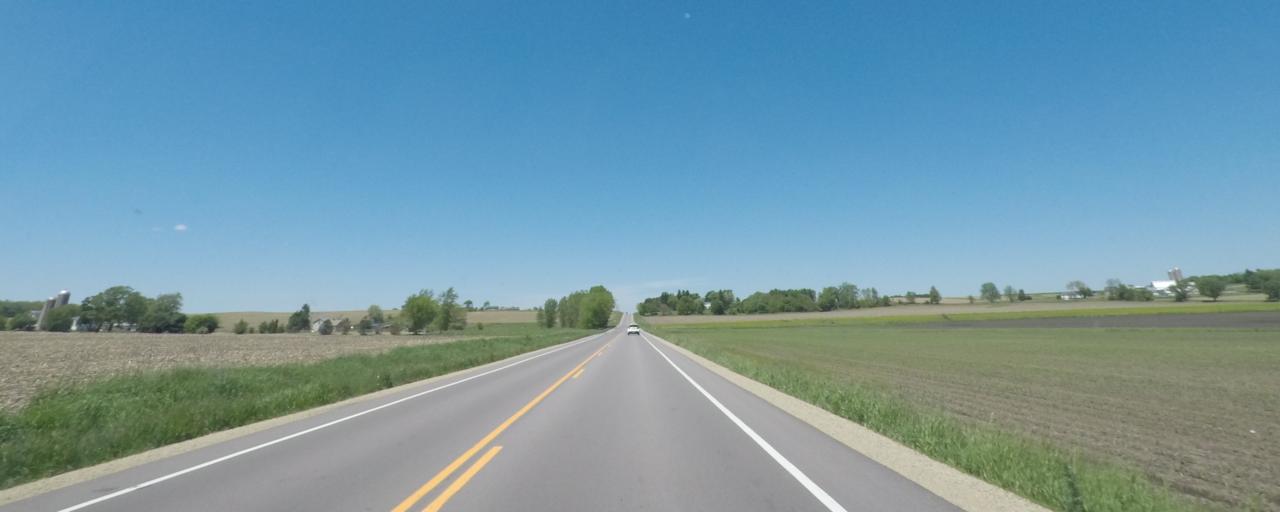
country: US
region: Wisconsin
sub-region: Green County
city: Brooklyn
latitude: 42.8173
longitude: -89.3694
